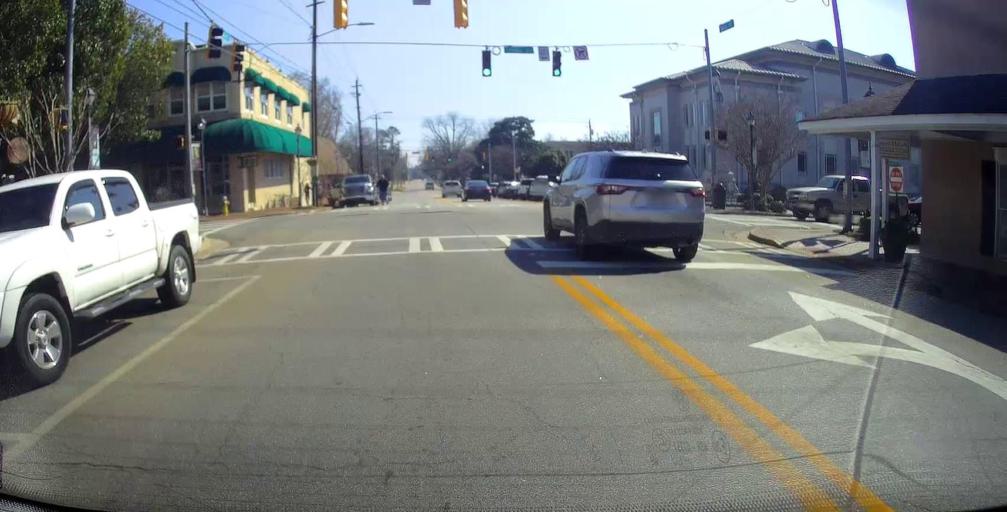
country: US
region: Georgia
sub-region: Houston County
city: Perry
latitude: 32.4584
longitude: -83.7337
